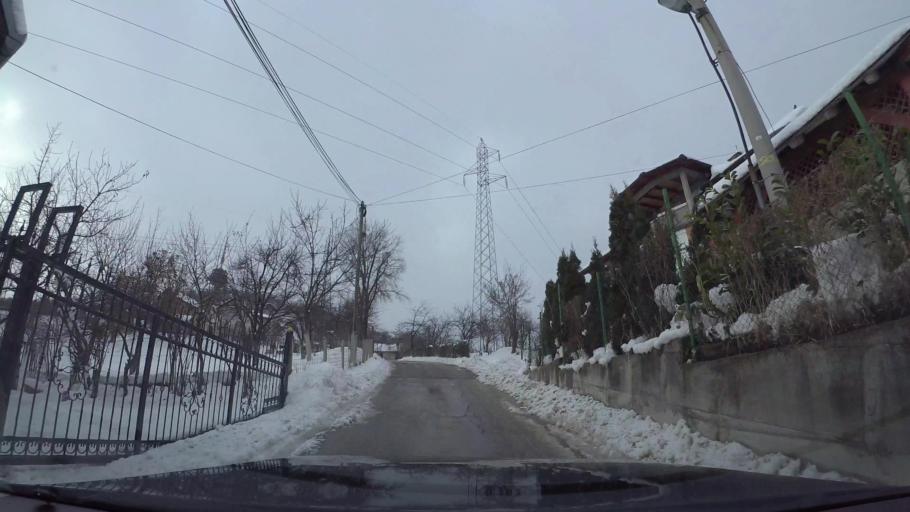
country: BA
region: Federation of Bosnia and Herzegovina
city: Kobilja Glava
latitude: 43.8725
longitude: 18.3924
